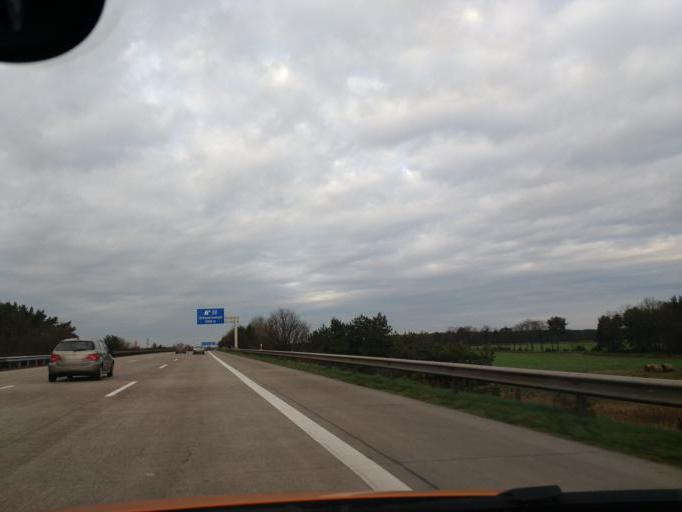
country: DE
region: Lower Saxony
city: Essel
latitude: 52.6640
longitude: 9.6981
